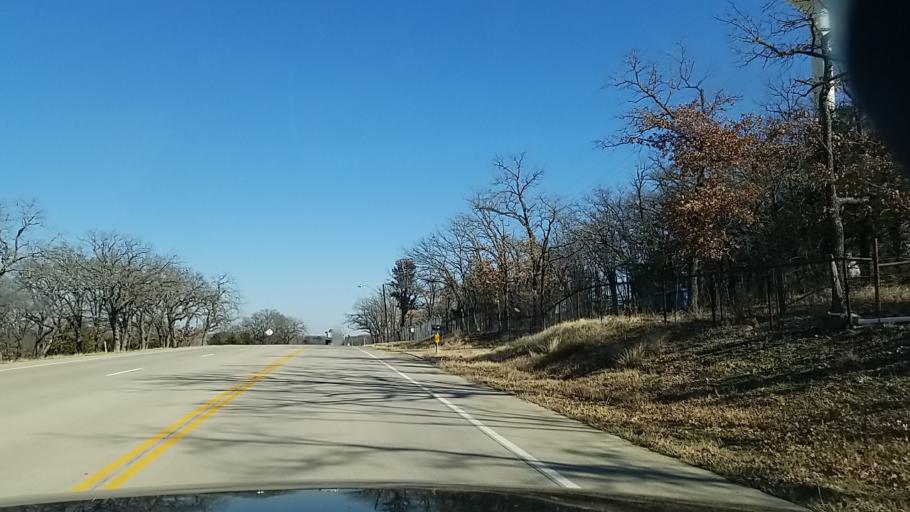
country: US
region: Texas
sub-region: Denton County
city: Argyle
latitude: 33.1290
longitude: -97.1783
